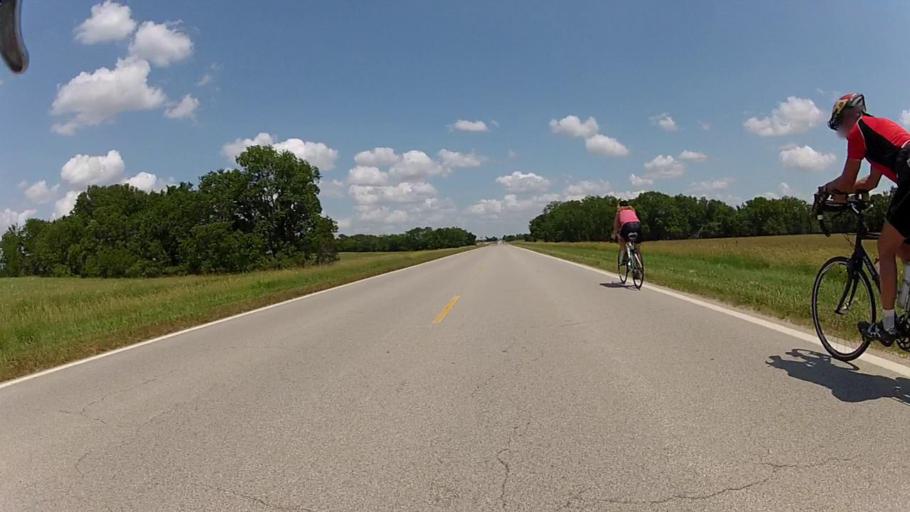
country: US
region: Kansas
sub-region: Labette County
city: Altamont
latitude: 37.1927
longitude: -95.3818
